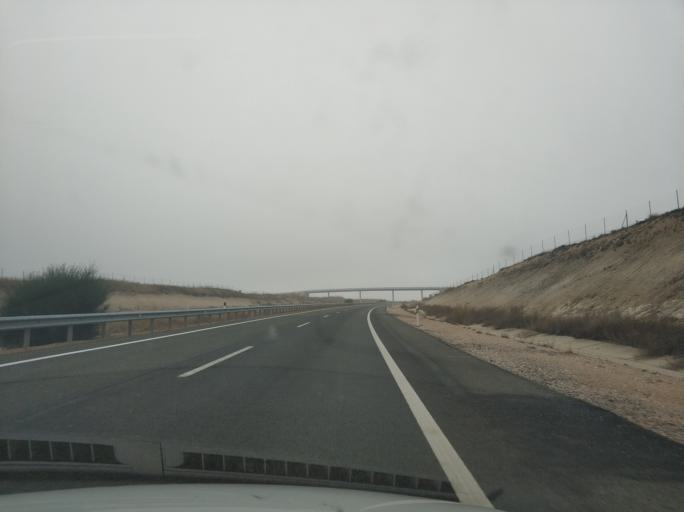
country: ES
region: Castille and Leon
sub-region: Provincia de Soria
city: Adradas
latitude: 41.3668
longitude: -2.4687
